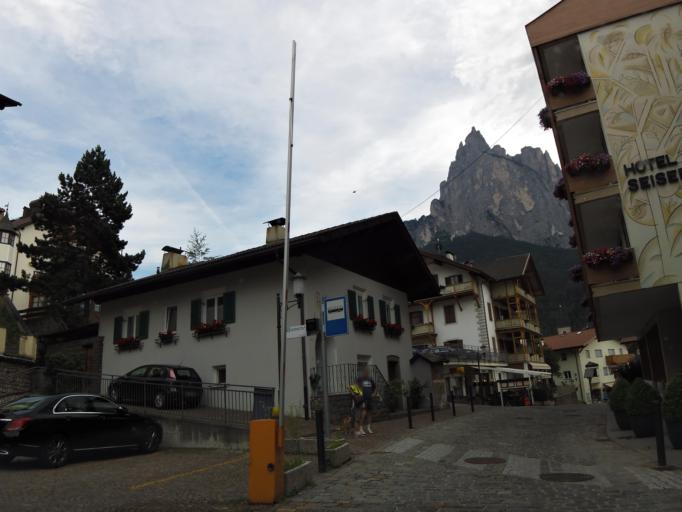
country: IT
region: Trentino-Alto Adige
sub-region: Bolzano
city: Siusi
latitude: 46.5460
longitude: 11.5597
